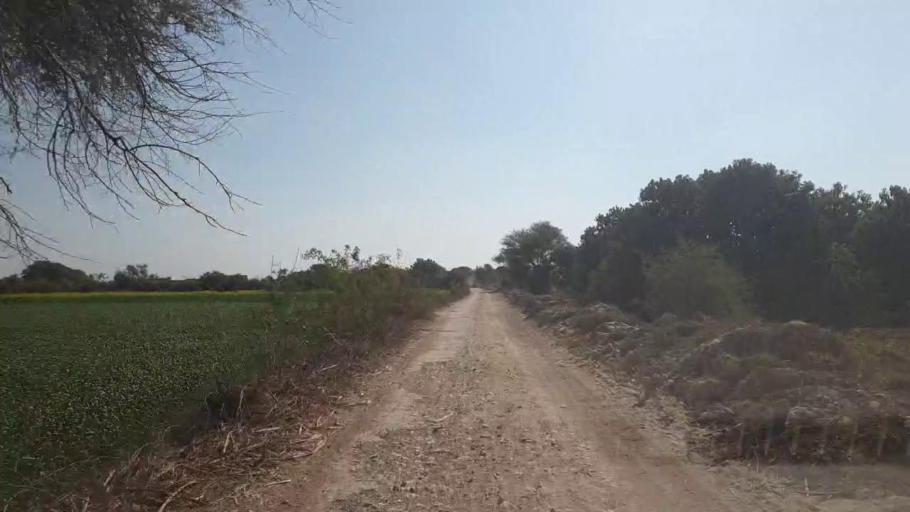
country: PK
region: Sindh
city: Chambar
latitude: 25.3128
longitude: 68.7408
